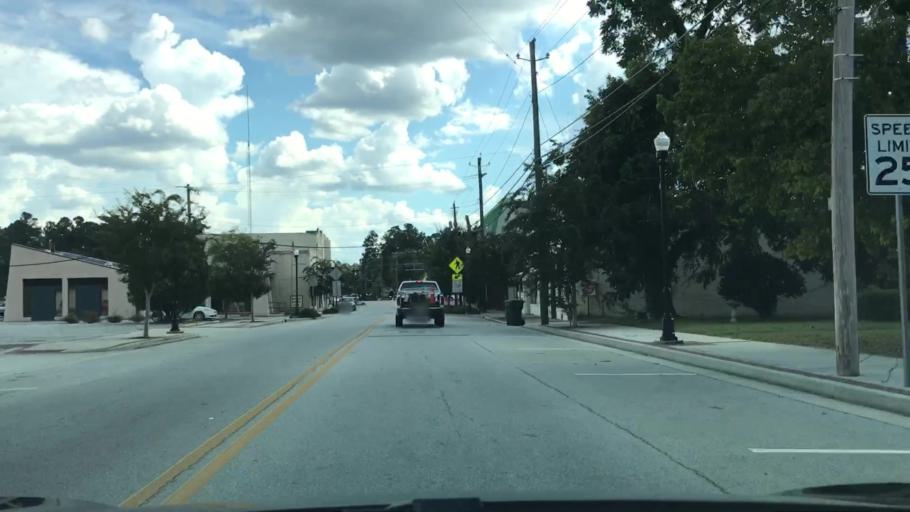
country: US
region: Georgia
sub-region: Jefferson County
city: Wadley
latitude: 32.8635
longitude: -82.4048
